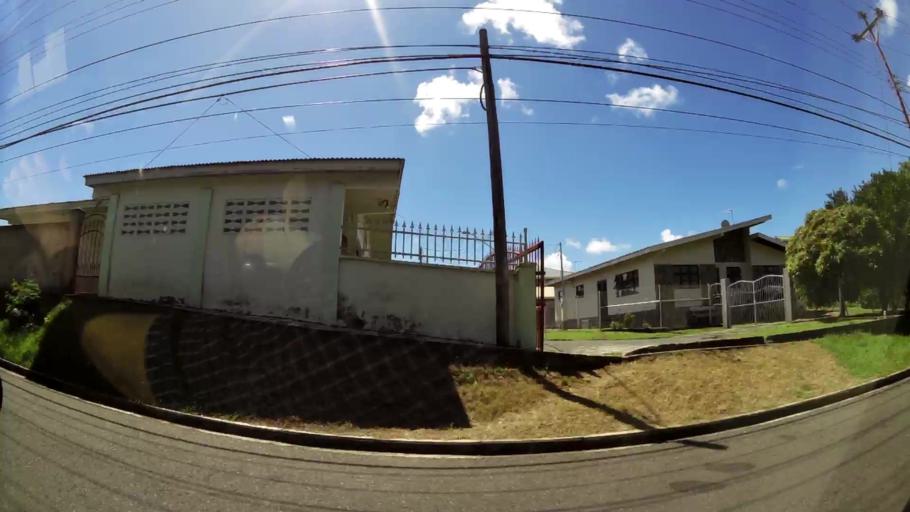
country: TT
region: Tobago
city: Scarborough
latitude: 11.1827
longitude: -60.8022
